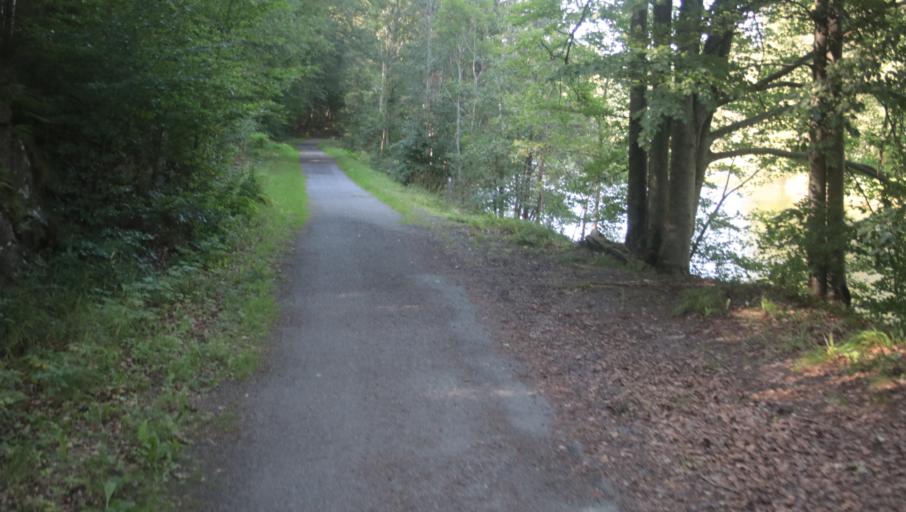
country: SE
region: Blekinge
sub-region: Karlshamns Kommun
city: Svangsta
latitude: 56.2671
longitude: 14.7648
